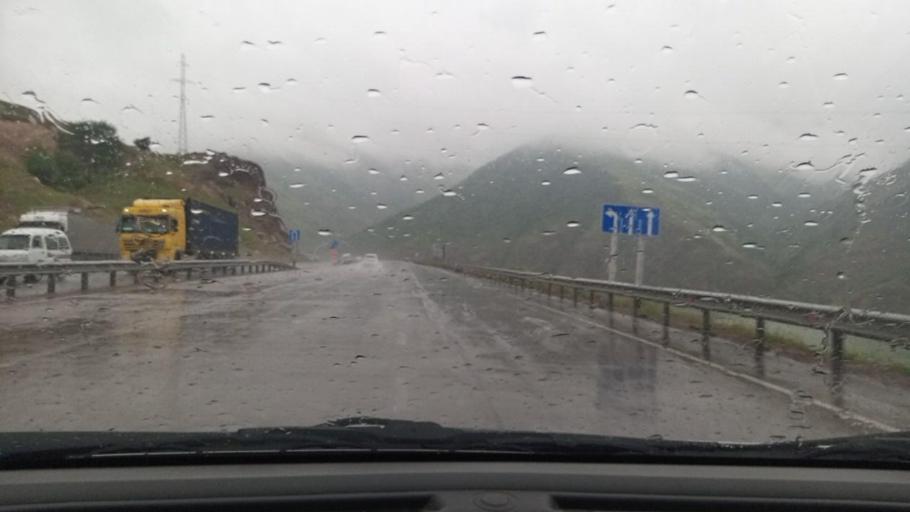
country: UZ
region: Toshkent
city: Angren
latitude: 41.0737
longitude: 70.2679
